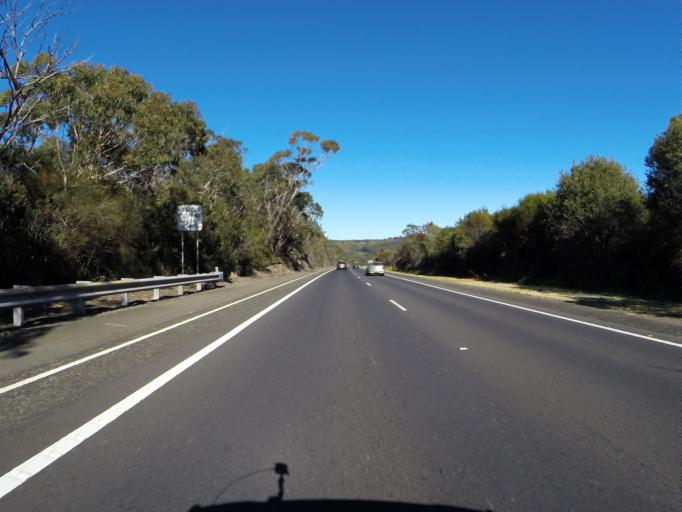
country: AU
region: New South Wales
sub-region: Wollongong
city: Helensburgh
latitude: -34.1547
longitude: 150.9875
